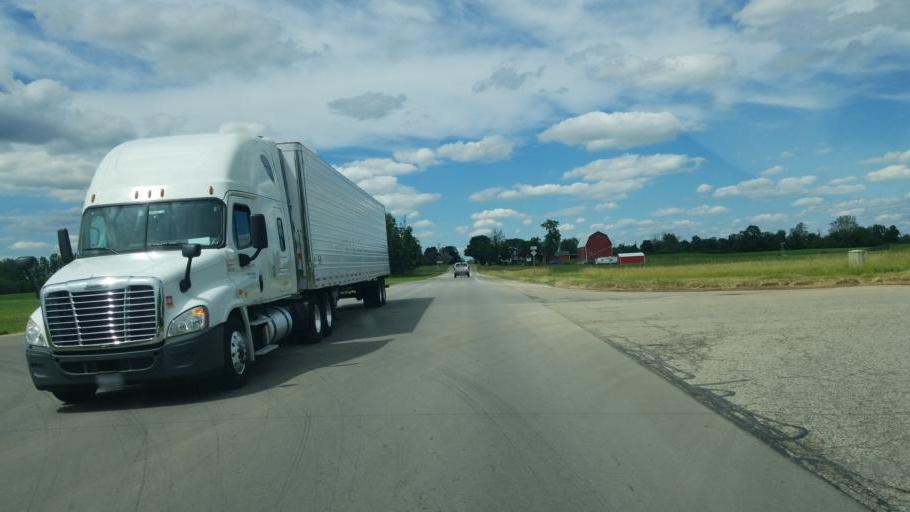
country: US
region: Michigan
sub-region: Eaton County
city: Charlotte
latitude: 42.5968
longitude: -84.8362
